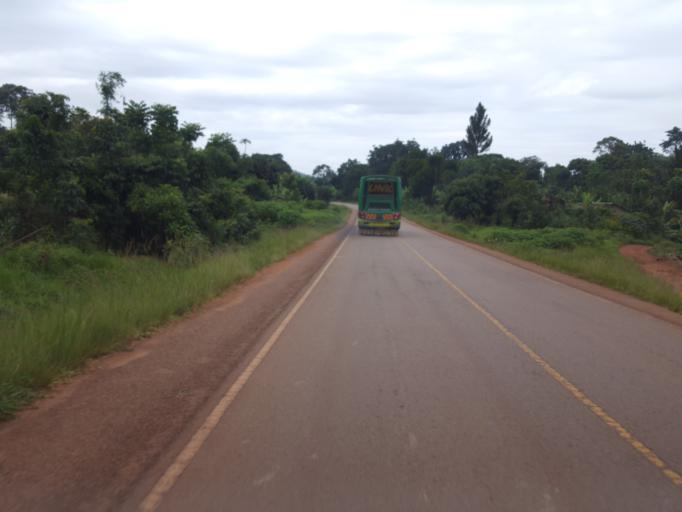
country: UG
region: Central Region
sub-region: Mityana District
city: Mityana
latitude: 0.6669
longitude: 32.0874
